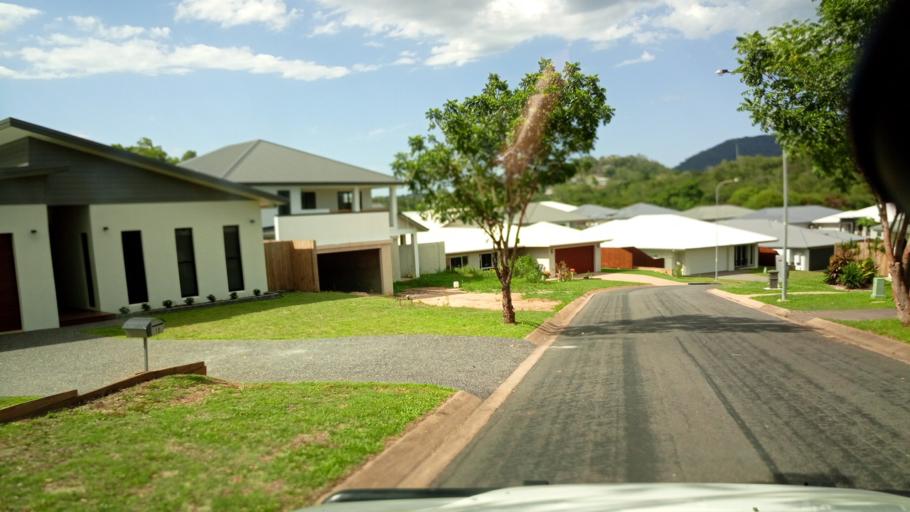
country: AU
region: Queensland
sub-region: Cairns
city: Woree
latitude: -16.9229
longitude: 145.7222
